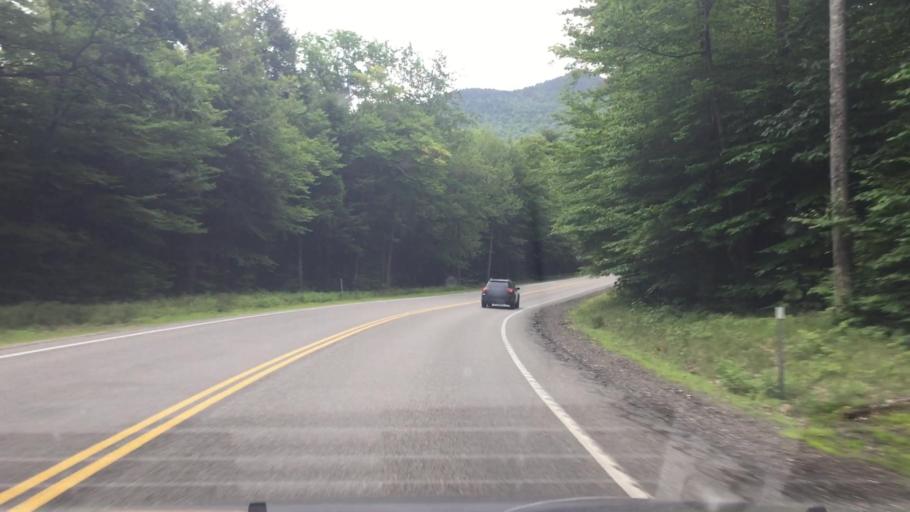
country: US
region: New Hampshire
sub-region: Carroll County
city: North Conway
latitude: 44.0787
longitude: -71.3430
